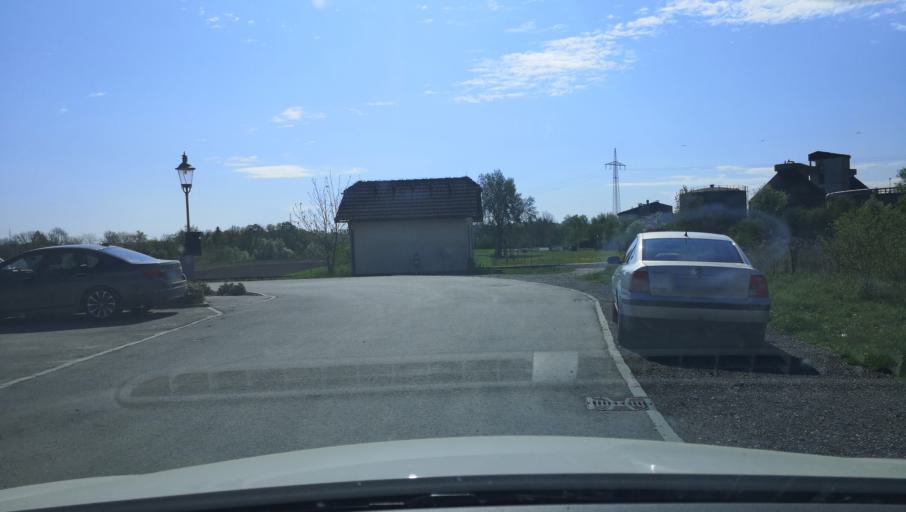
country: AT
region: Lower Austria
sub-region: Politischer Bezirk Melk
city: Petzenkirchen
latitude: 48.1399
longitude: 15.1518
